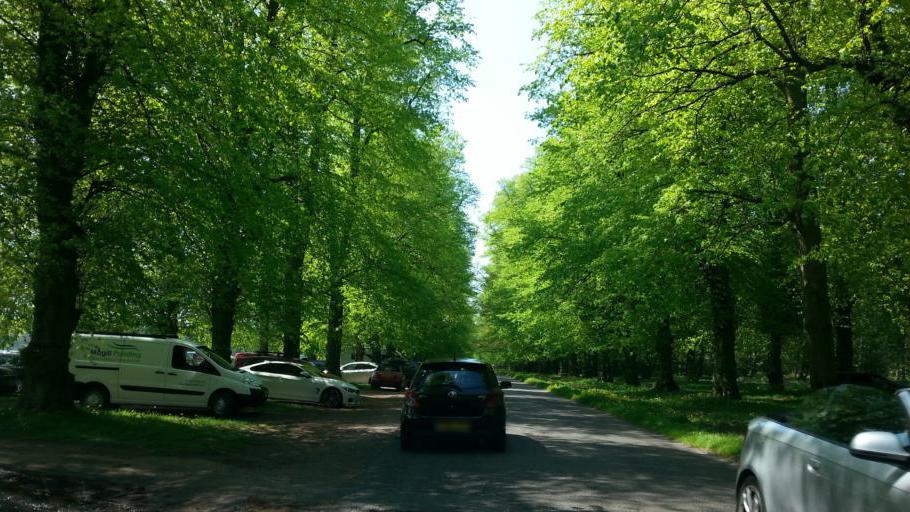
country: GB
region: England
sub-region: Nottinghamshire
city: Babworth
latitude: 53.2875
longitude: -1.0434
